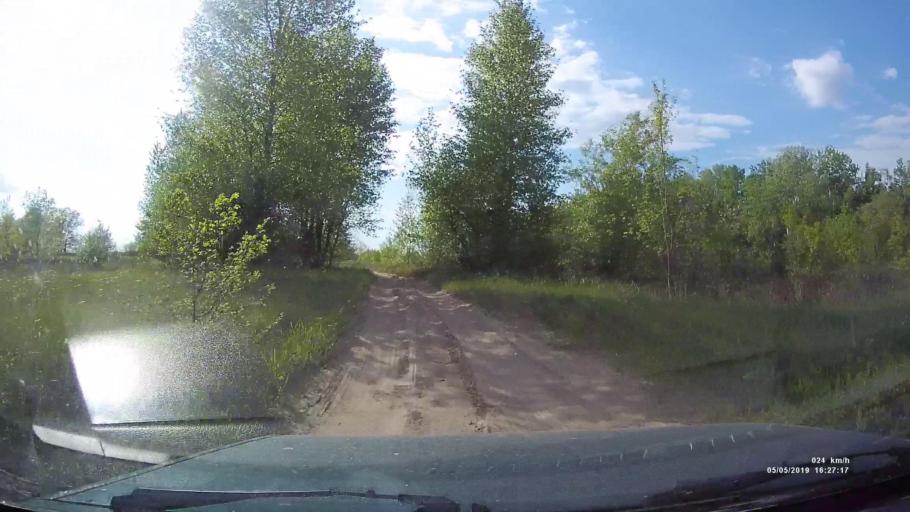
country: RU
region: Rostov
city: Ust'-Donetskiy
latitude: 47.7648
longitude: 41.0193
